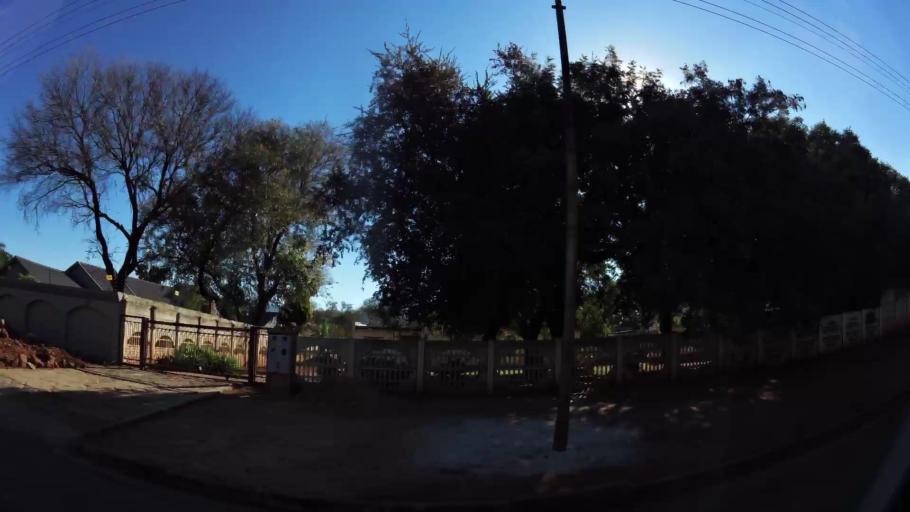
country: ZA
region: Limpopo
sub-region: Waterberg District Municipality
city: Mokopane
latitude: -24.1849
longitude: 28.9967
